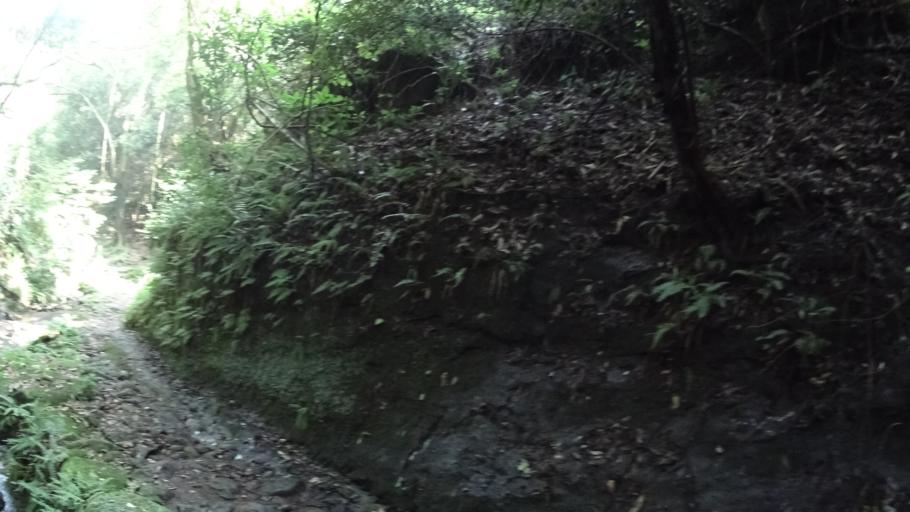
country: JP
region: Kanagawa
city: Zushi
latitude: 35.3052
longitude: 139.6054
